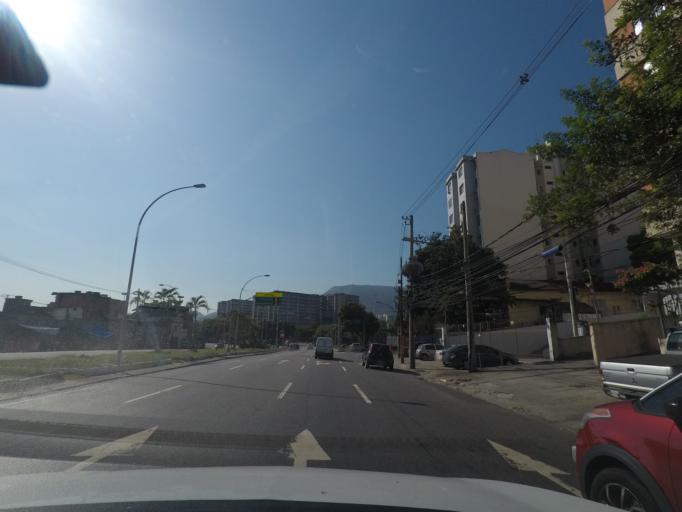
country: BR
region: Rio de Janeiro
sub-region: Rio De Janeiro
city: Rio de Janeiro
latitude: -22.9079
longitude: -43.2389
